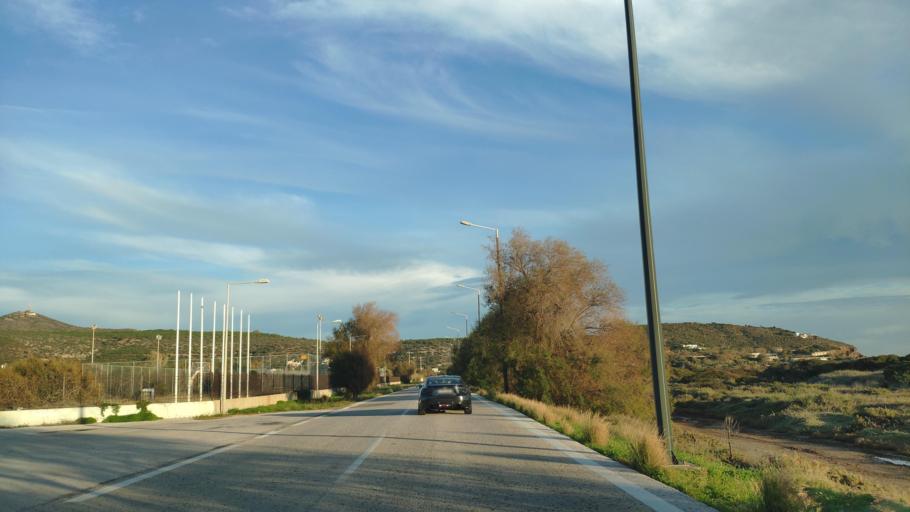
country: GR
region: Attica
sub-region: Nomarchia Anatolikis Attikis
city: Palaia Fokaia
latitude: 37.6632
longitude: 23.9940
